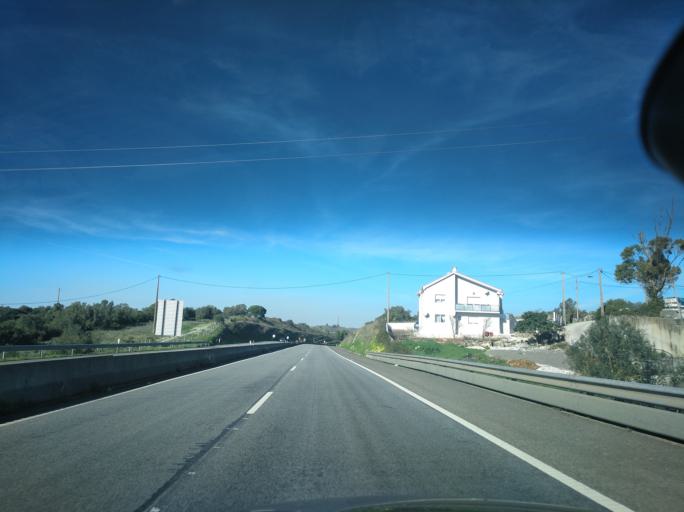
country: PT
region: Lisbon
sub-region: Sintra
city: Pero Pinheiro
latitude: 38.8501
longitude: -9.3495
